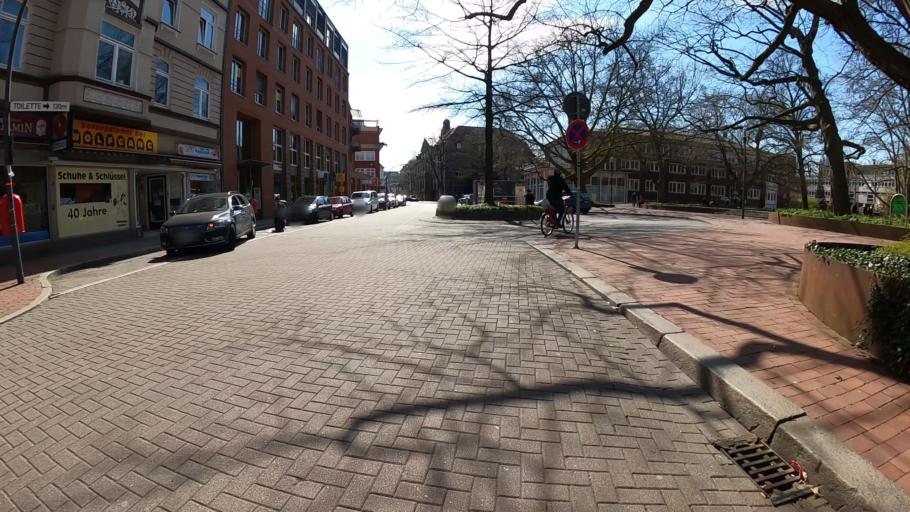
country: DE
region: Hamburg
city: Harburg
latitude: 53.4596
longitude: 9.9809
